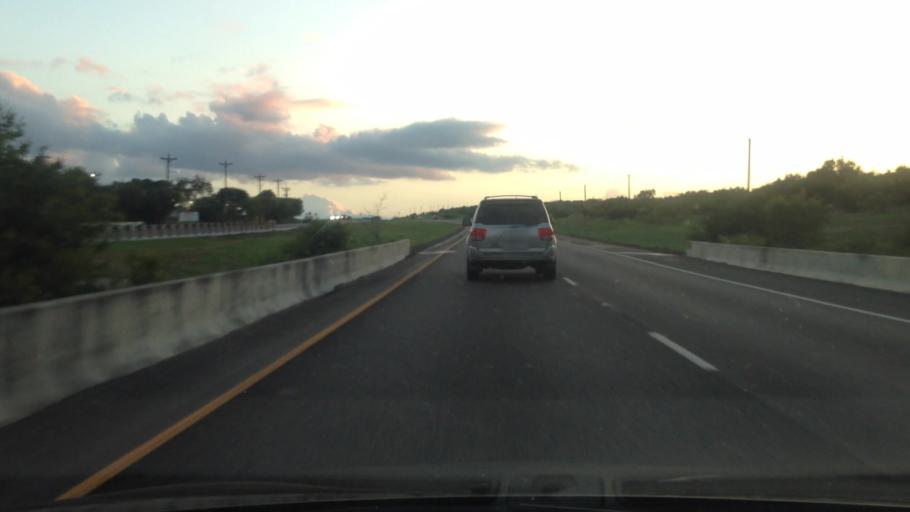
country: US
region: Texas
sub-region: Parker County
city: Aledo
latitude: 32.5975
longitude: -97.5759
